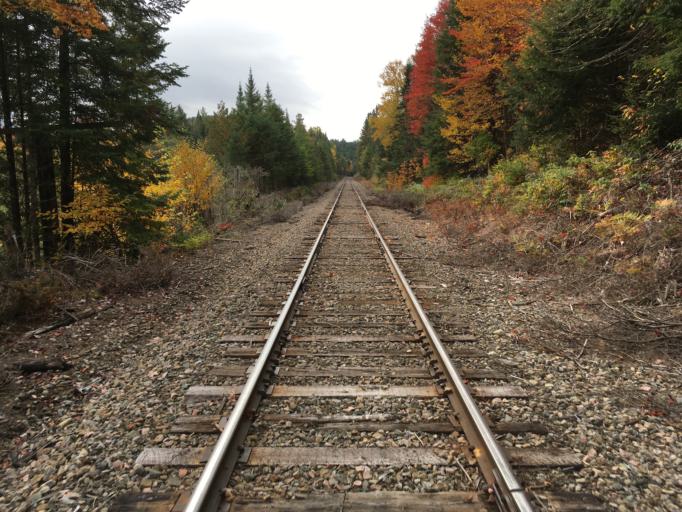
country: US
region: Vermont
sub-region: Caledonia County
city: Lyndonville
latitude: 44.6206
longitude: -71.9665
